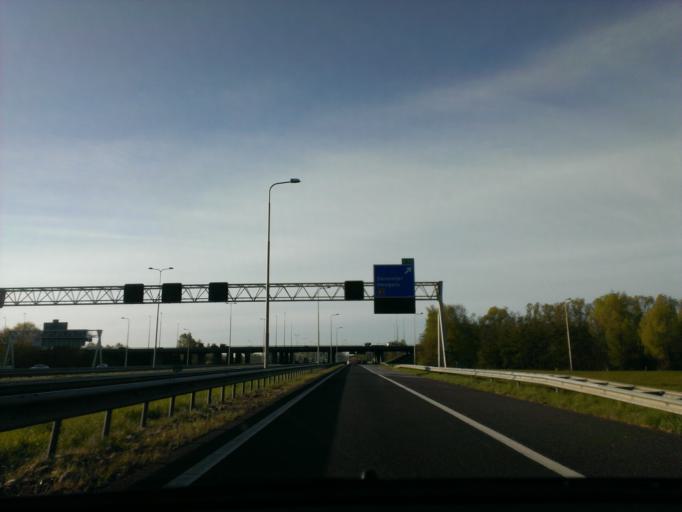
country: NL
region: Gelderland
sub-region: Gemeente Apeldoorn
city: Apeldoorn
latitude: 52.1898
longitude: 6.0210
